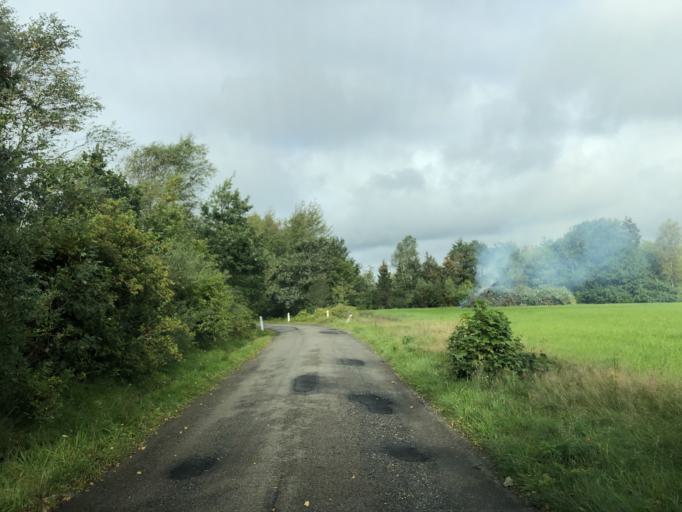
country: DK
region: Central Jutland
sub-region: Holstebro Kommune
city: Ulfborg
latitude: 56.2971
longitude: 8.4504
